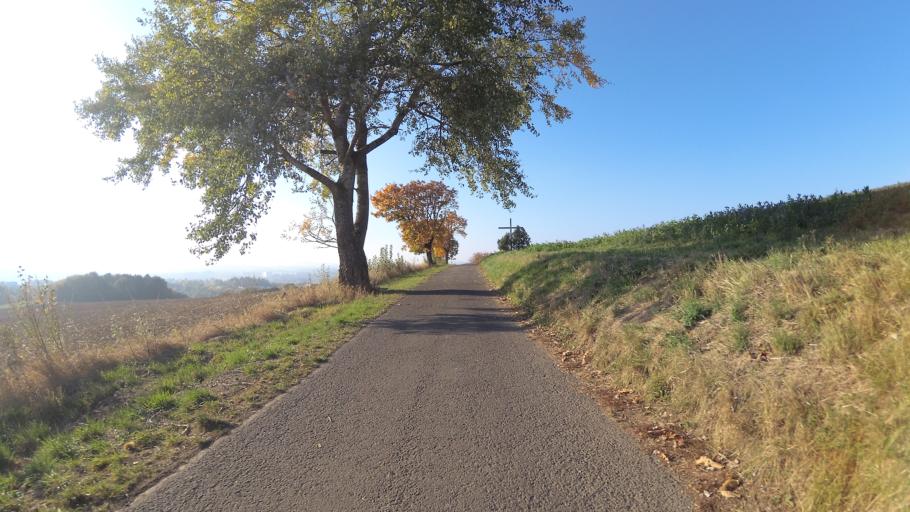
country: DE
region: Saarland
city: Sankt Wendel
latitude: 49.4568
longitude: 7.1899
